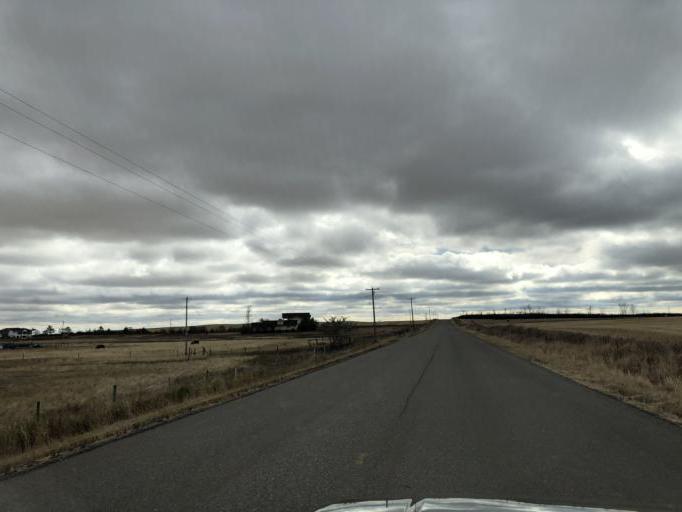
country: CA
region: Alberta
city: Chestermere
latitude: 50.9178
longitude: -113.8830
